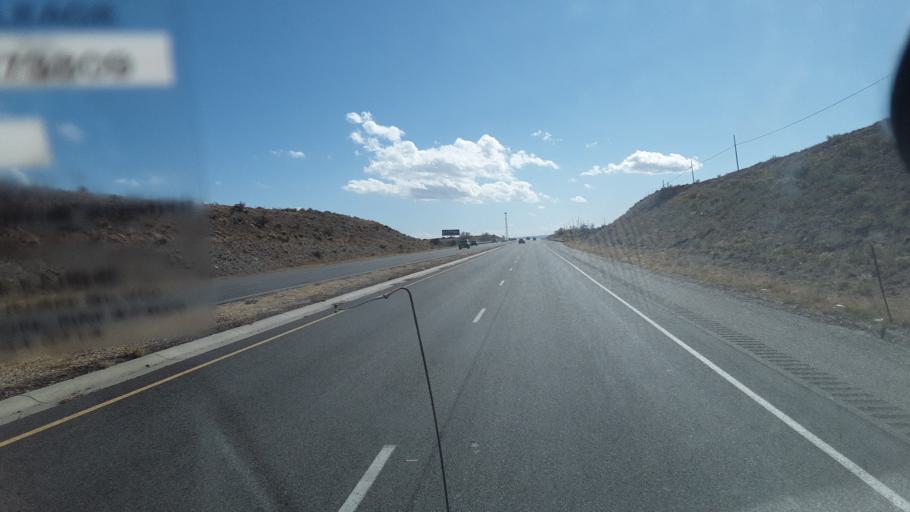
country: US
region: New Mexico
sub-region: Rio Arriba County
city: Ohkay Owingeh
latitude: 36.0262
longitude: -106.0926
